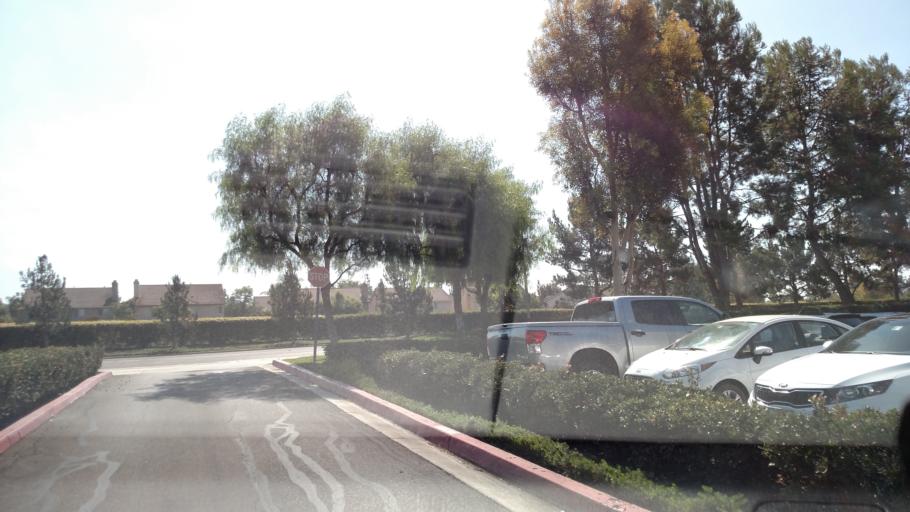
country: US
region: California
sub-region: Orange County
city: Tustin
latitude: 33.7135
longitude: -117.7968
